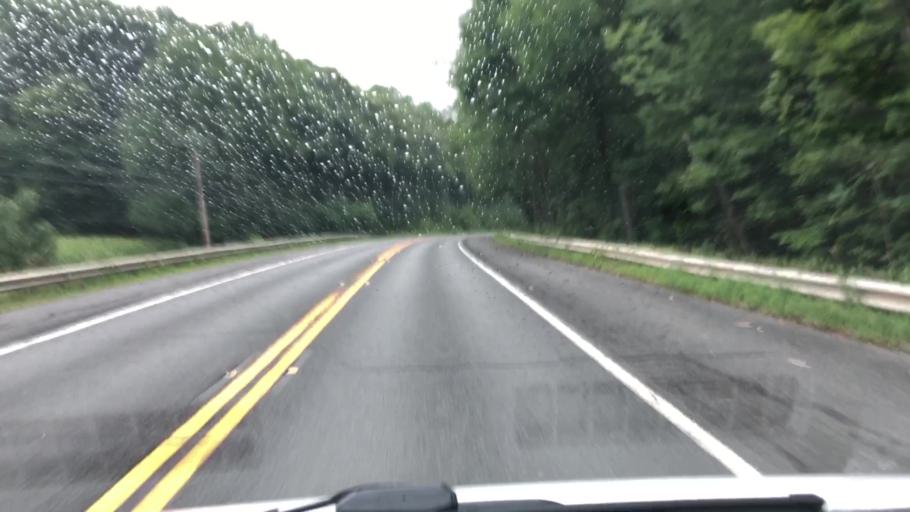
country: US
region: Massachusetts
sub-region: Berkshire County
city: Lanesborough
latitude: 42.5817
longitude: -73.2509
